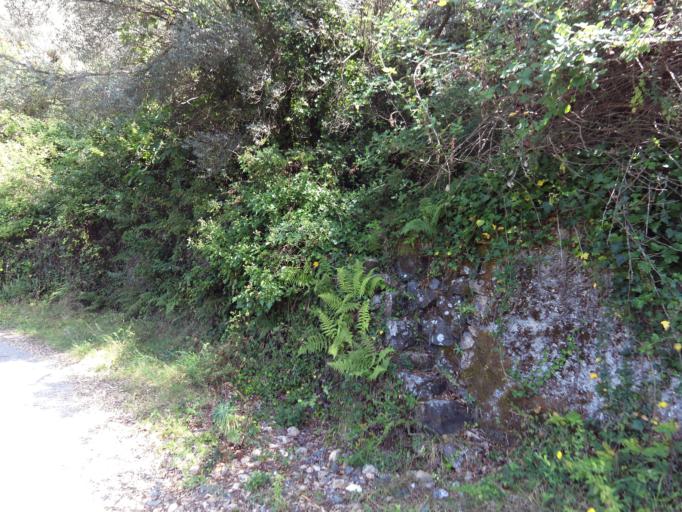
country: IT
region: Calabria
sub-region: Provincia di Reggio Calabria
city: Pazzano
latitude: 38.4735
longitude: 16.4421
